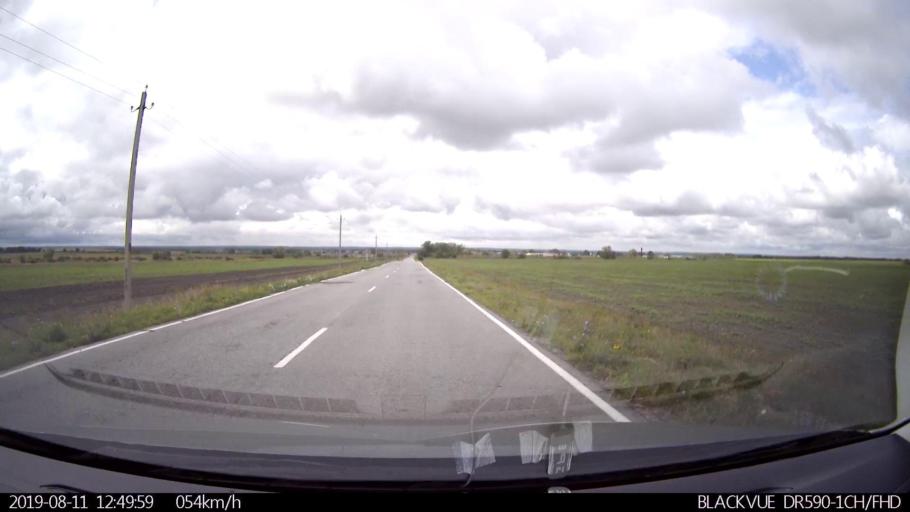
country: RU
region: Ulyanovsk
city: Ignatovka
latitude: 53.8750
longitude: 47.6791
